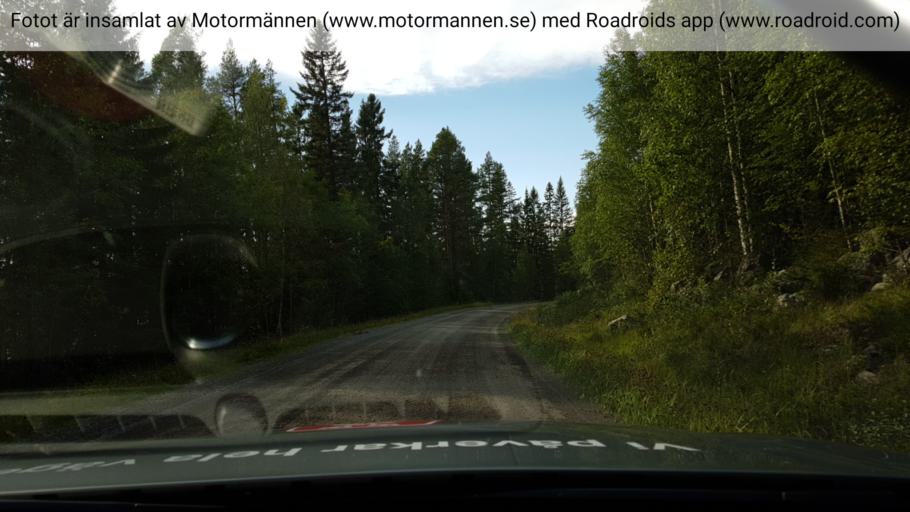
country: SE
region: Jaemtland
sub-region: Braecke Kommun
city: Braecke
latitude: 63.2114
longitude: 15.3757
